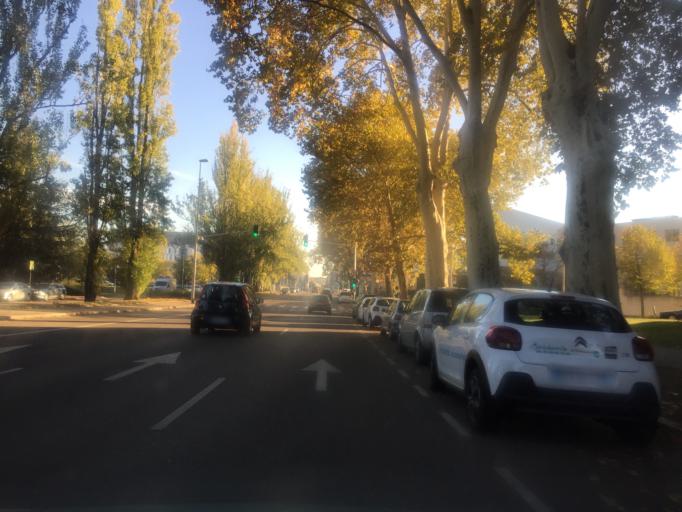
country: FR
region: Alsace
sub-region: Departement du Bas-Rhin
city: Strasbourg
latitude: 48.5739
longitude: 7.7500
